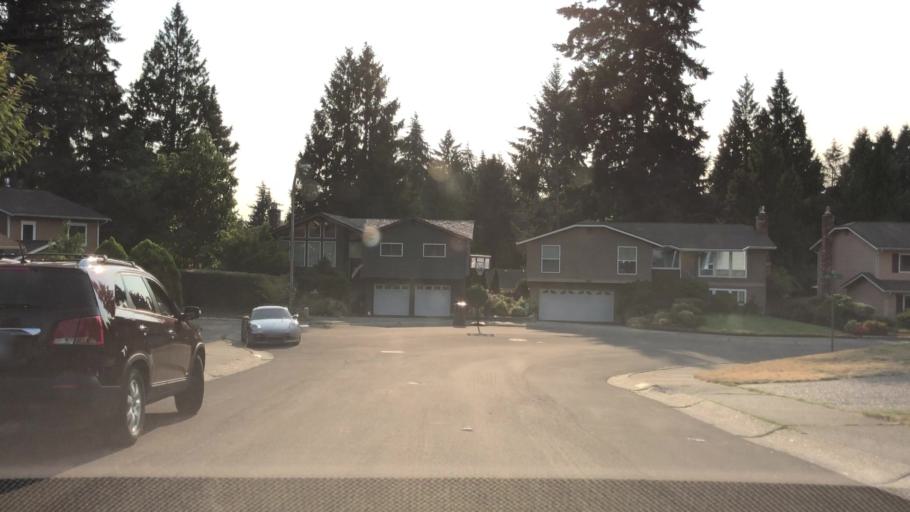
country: US
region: Washington
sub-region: King County
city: Kingsgate
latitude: 47.6981
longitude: -122.1692
